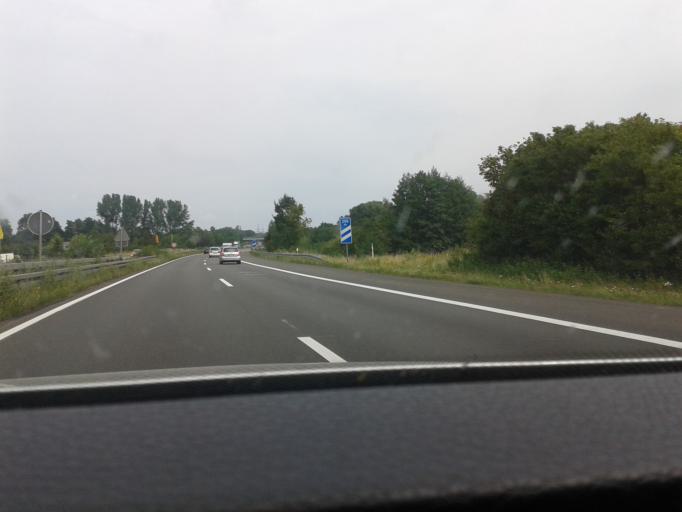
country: DE
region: Lower Saxony
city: Wolfsburg
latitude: 52.3832
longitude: 10.7298
